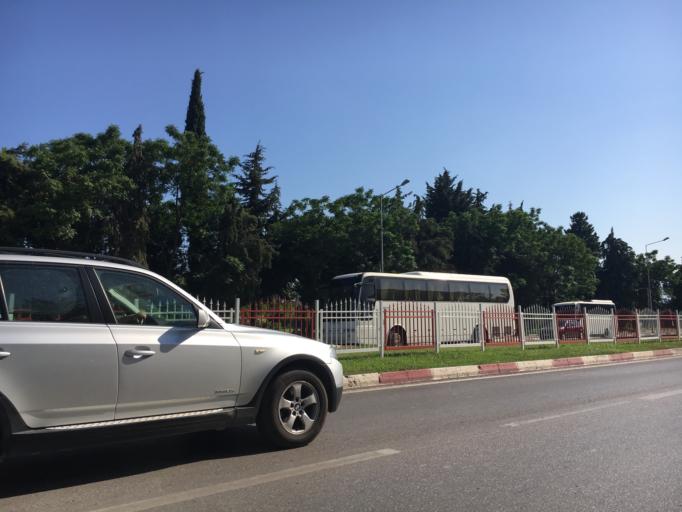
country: TR
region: Antalya
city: Antalya
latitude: 36.8868
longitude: 30.6712
